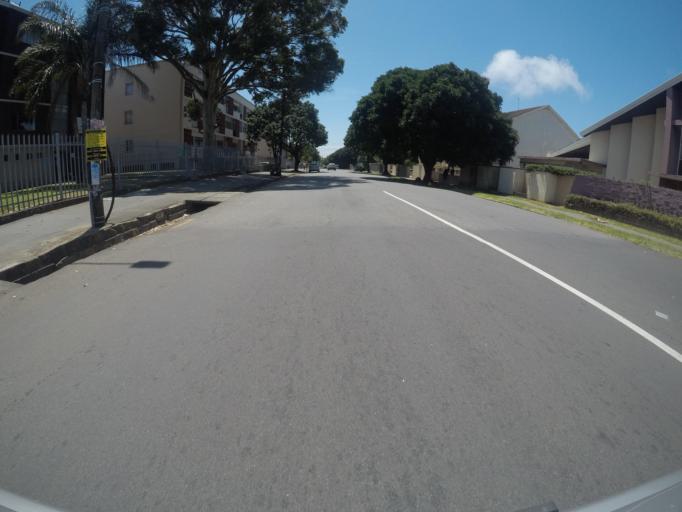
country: ZA
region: Eastern Cape
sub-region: Buffalo City Metropolitan Municipality
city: East London
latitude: -33.0048
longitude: 27.9040
